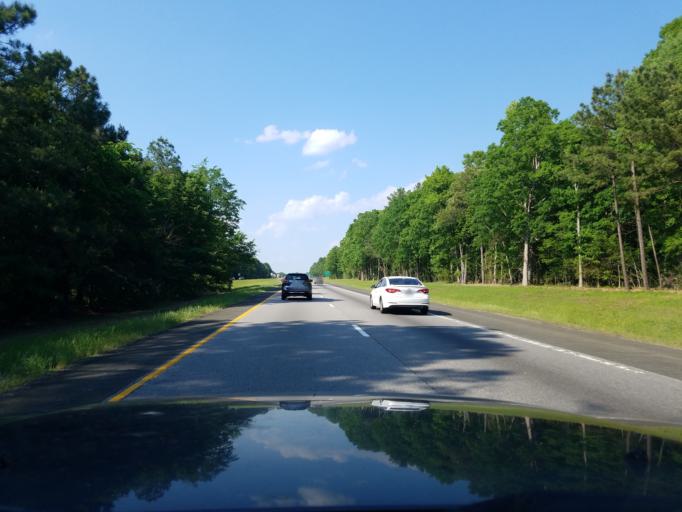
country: US
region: North Carolina
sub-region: Granville County
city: Butner
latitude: 36.1079
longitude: -78.7522
